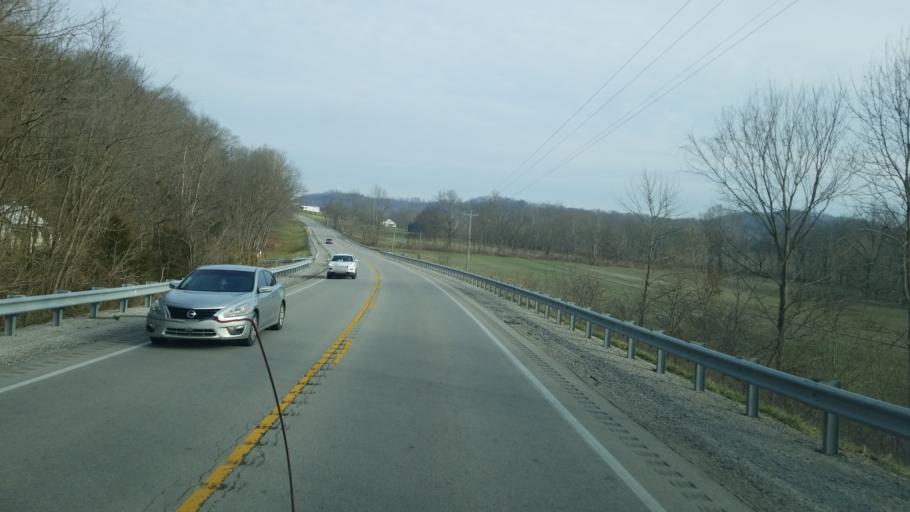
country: US
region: Kentucky
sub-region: Casey County
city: Liberty
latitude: 37.3551
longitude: -84.8687
